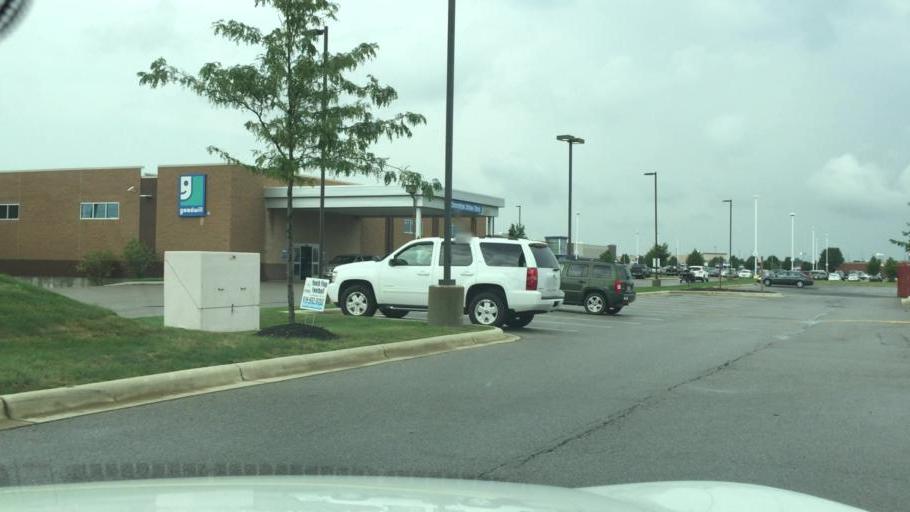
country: US
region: Ohio
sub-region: Franklin County
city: Lincoln Village
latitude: 39.9816
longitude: -83.1530
